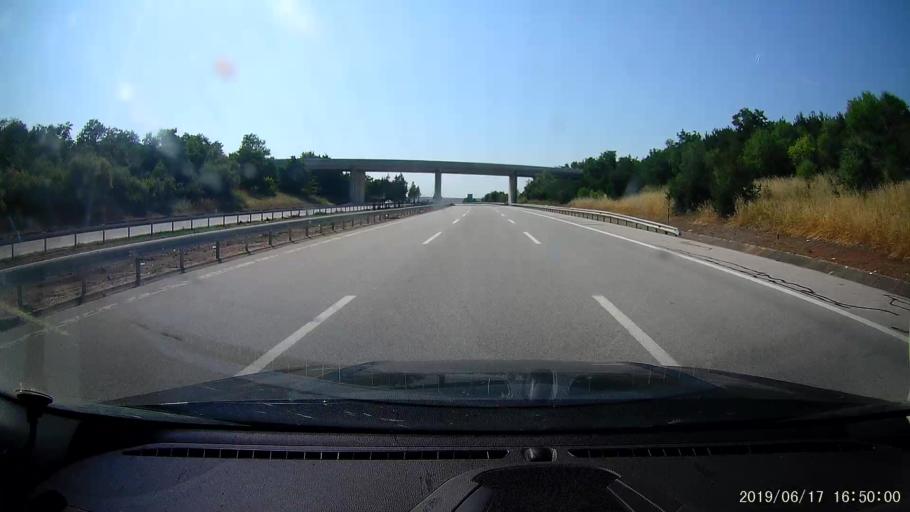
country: TR
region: Kirklareli
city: Babaeski
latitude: 41.5180
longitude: 27.1007
